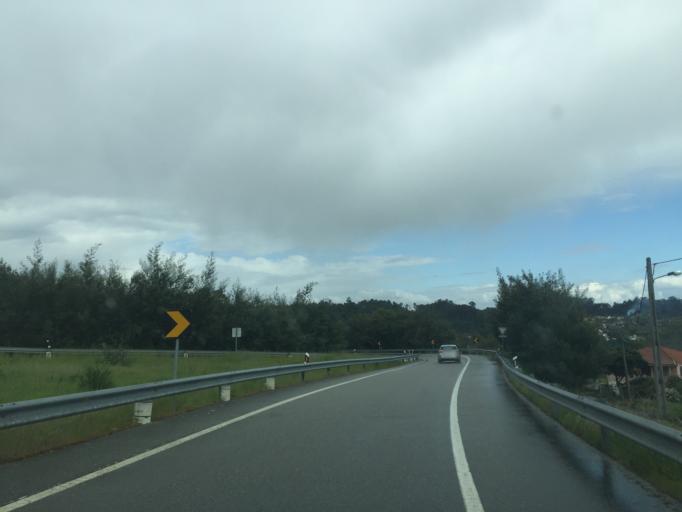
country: PT
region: Viseu
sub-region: Viseu
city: Abraveses
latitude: 40.6680
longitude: -7.9911
